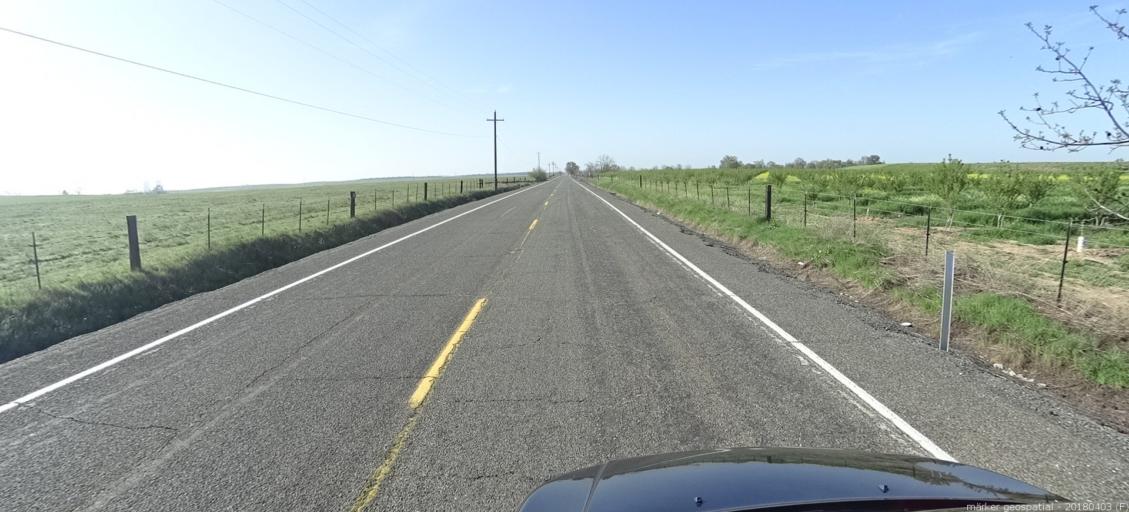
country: US
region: California
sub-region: Sacramento County
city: Clay
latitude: 38.3911
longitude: -121.1685
